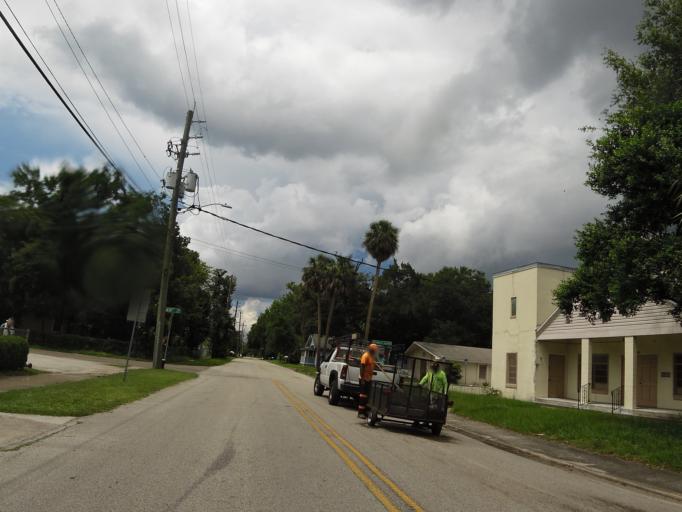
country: US
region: Florida
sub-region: Duval County
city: Jacksonville
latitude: 30.3829
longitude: -81.6412
